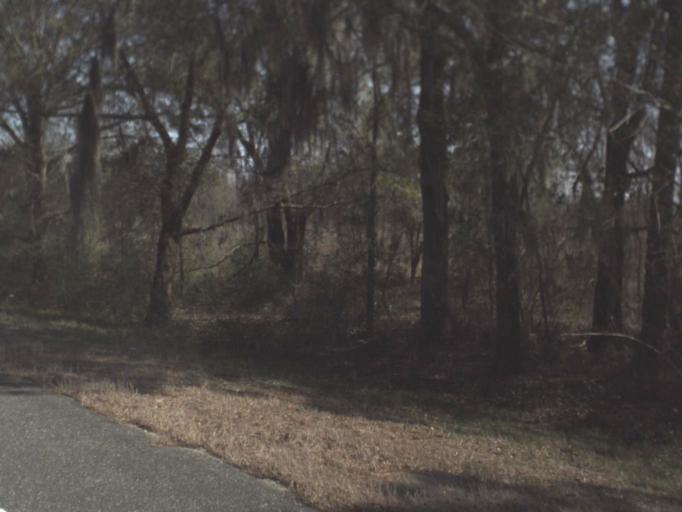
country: US
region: Florida
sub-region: Gadsden County
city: Gretna
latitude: 30.5291
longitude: -84.7854
